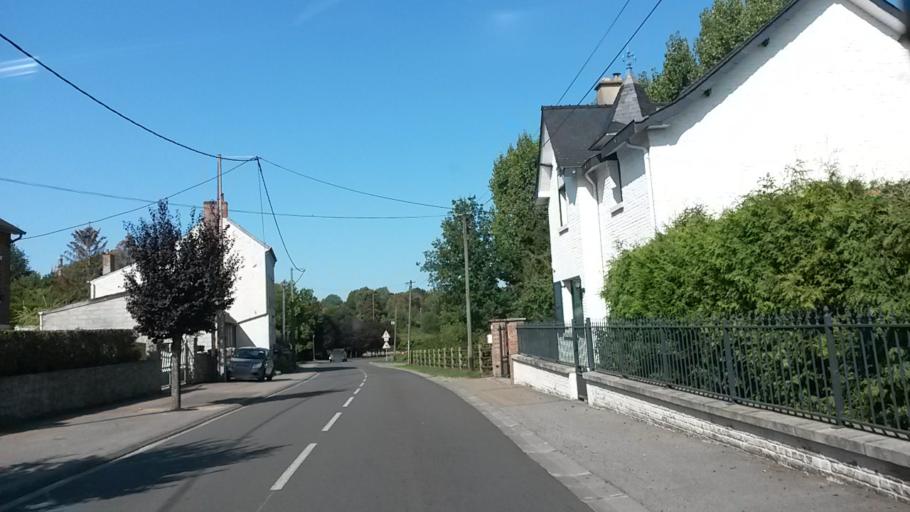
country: FR
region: Nord-Pas-de-Calais
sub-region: Departement du Nord
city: Avesnelles
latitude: 50.1226
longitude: 3.9418
